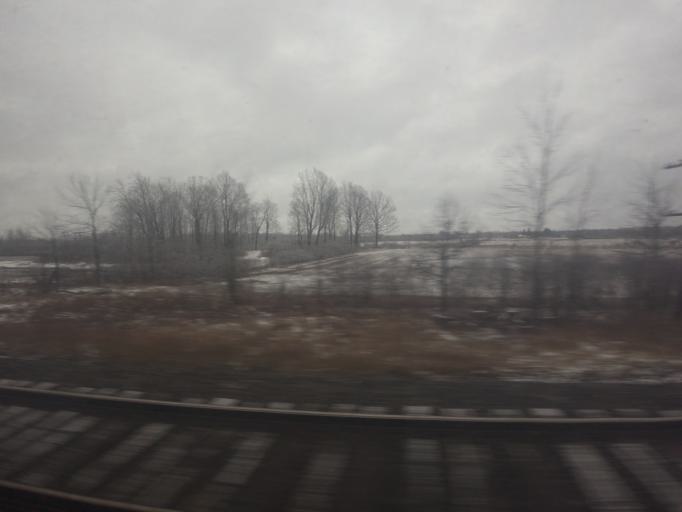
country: US
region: New York
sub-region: Jefferson County
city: Alexandria Bay
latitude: 44.4149
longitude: -75.9983
